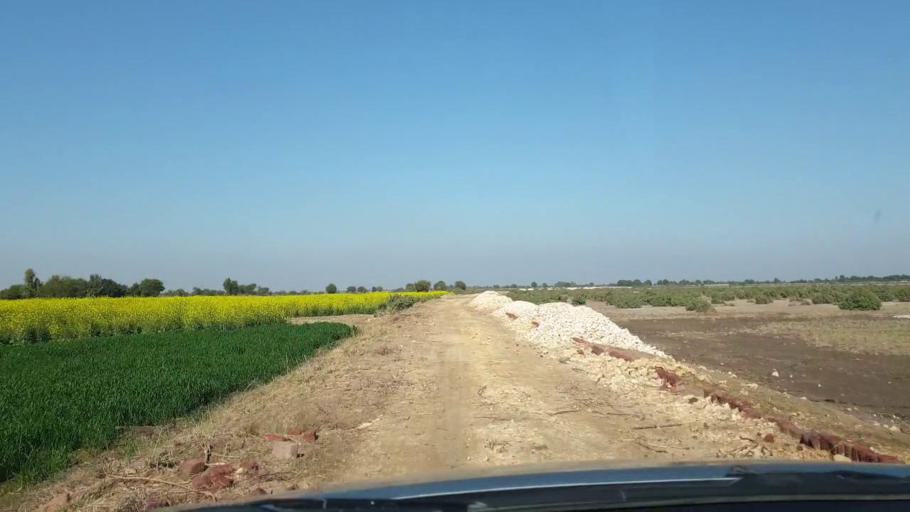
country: PK
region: Sindh
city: Jhol
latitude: 25.9240
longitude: 68.9445
